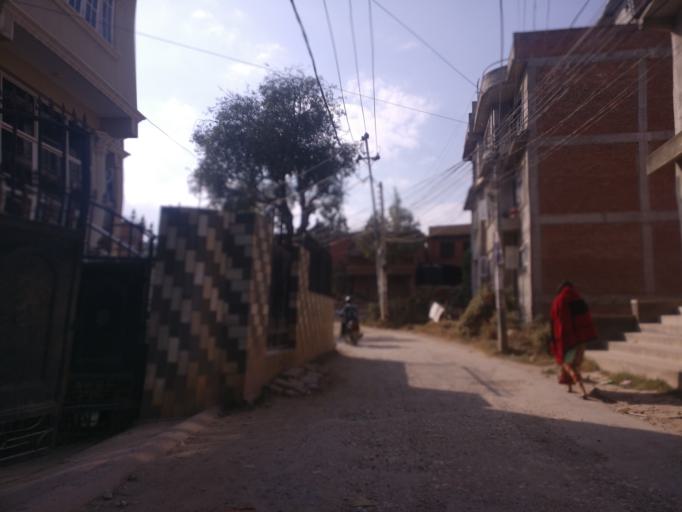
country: NP
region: Central Region
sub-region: Bagmati Zone
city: Patan
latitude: 27.6787
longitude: 85.3298
